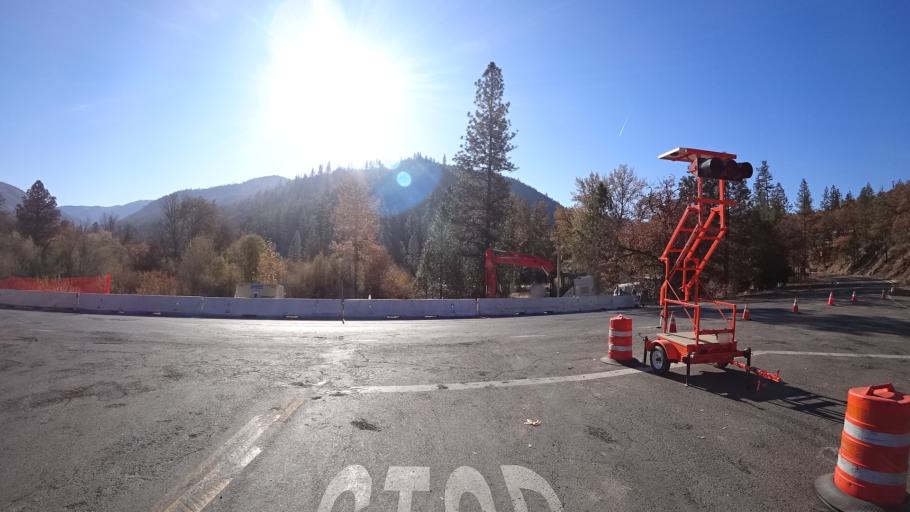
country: US
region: California
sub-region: Siskiyou County
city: Yreka
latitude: 41.8702
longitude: -122.8176
